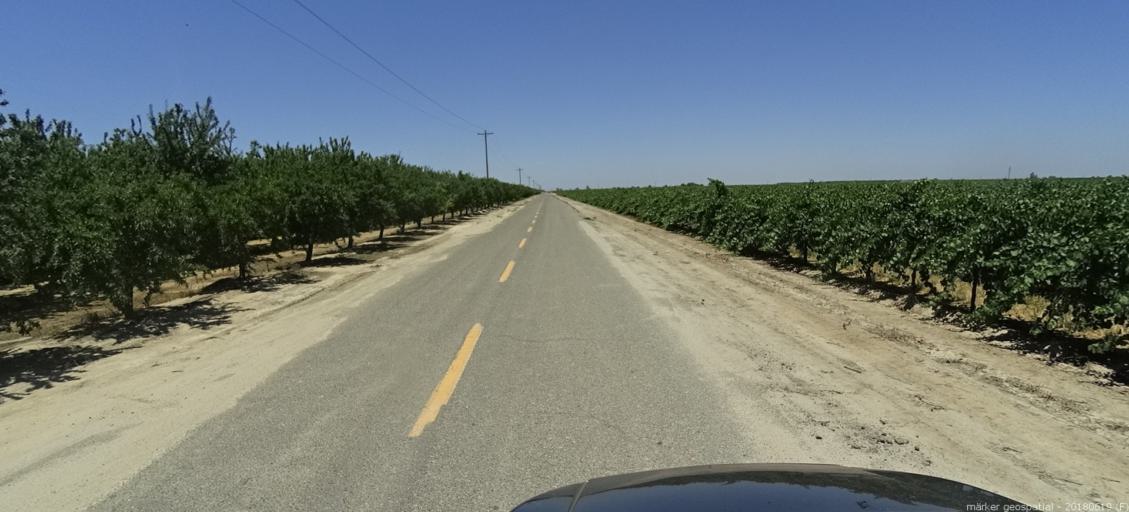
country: US
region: California
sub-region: Madera County
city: Parkwood
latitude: 36.8658
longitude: -120.1560
